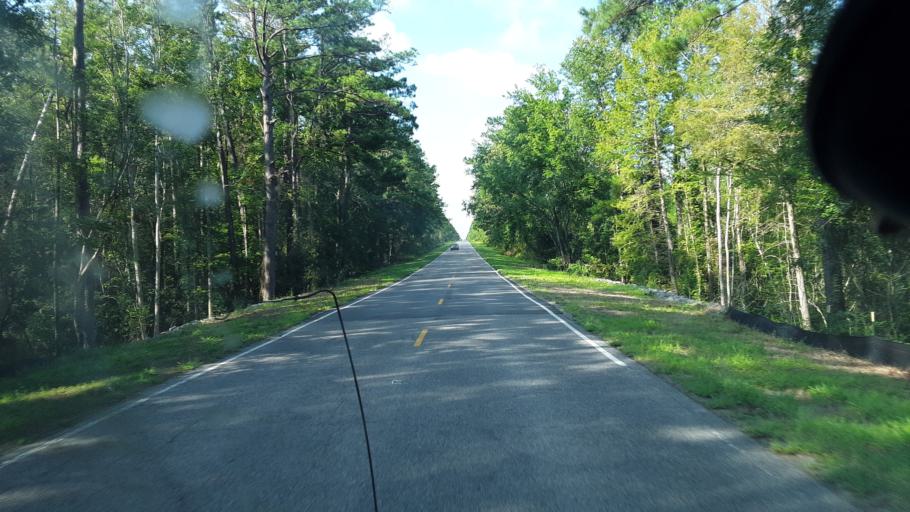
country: US
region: North Carolina
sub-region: Brunswick County
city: Boiling Spring Lakes
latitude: 34.0397
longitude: -78.0077
